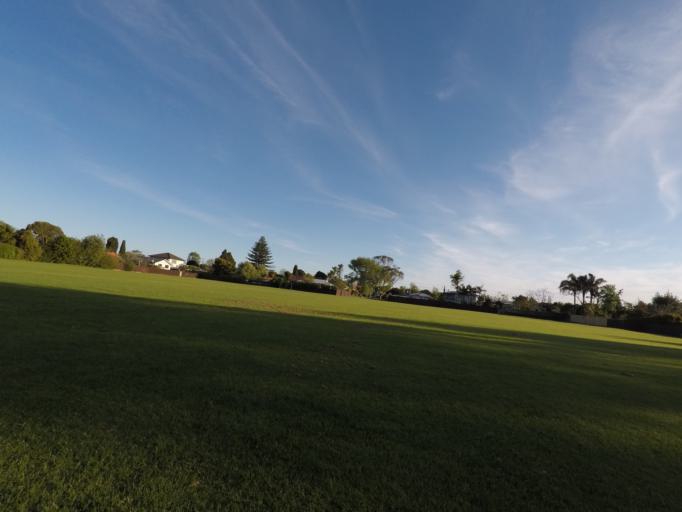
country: NZ
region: Auckland
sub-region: Auckland
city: Rosebank
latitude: -36.8427
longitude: 174.6488
